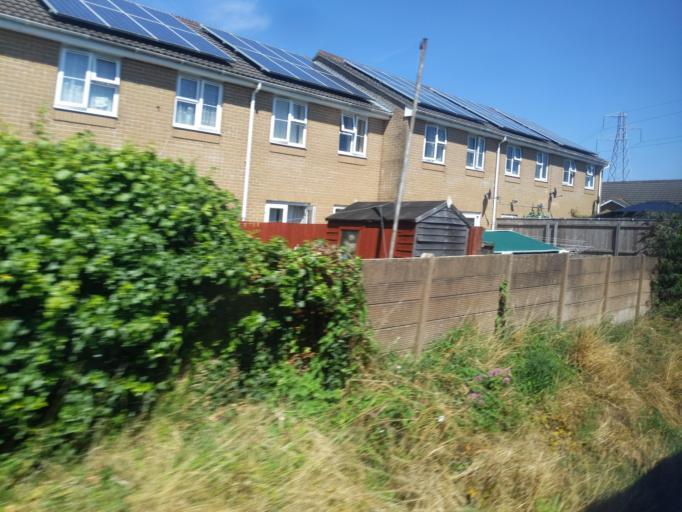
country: GB
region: England
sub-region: Plymouth
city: Plymstock
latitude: 50.3829
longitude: -4.1061
